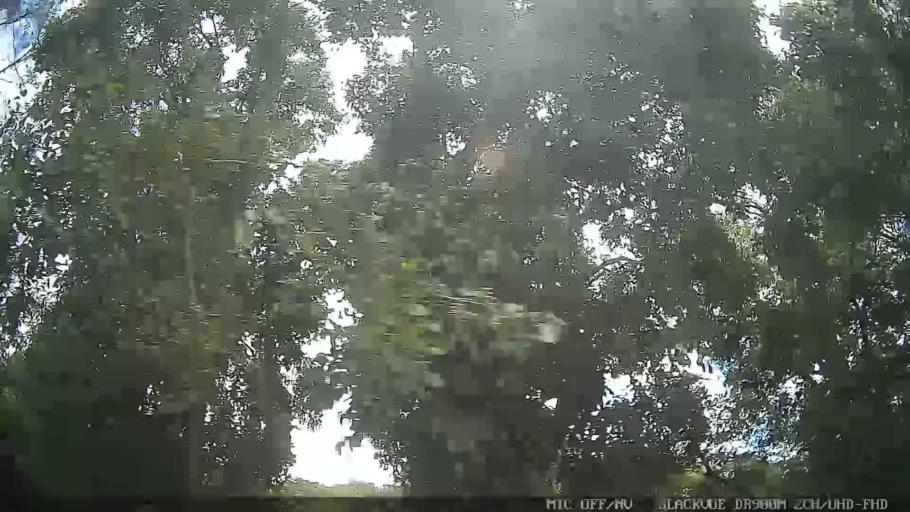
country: BR
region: Sao Paulo
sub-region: Pedreira
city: Pedreira
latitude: -22.7397
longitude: -46.9214
